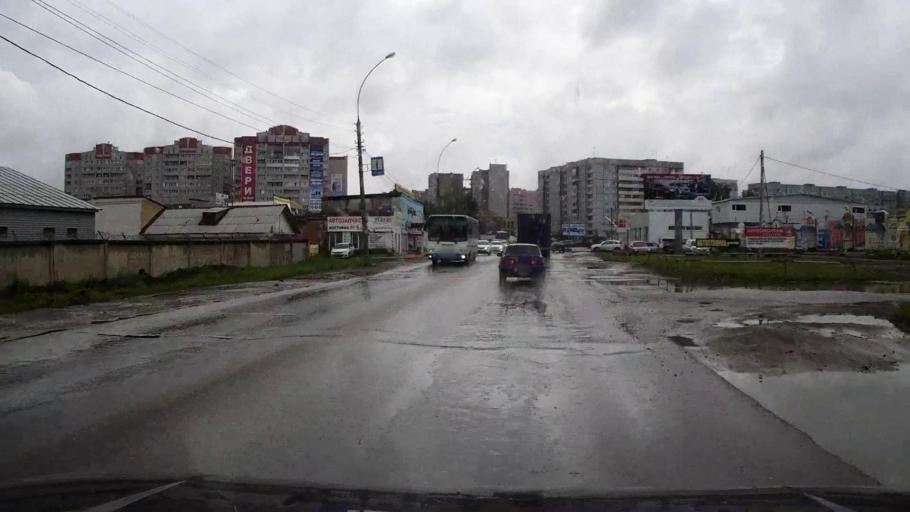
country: RU
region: Vologda
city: Vologda
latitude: 59.2046
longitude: 39.8658
